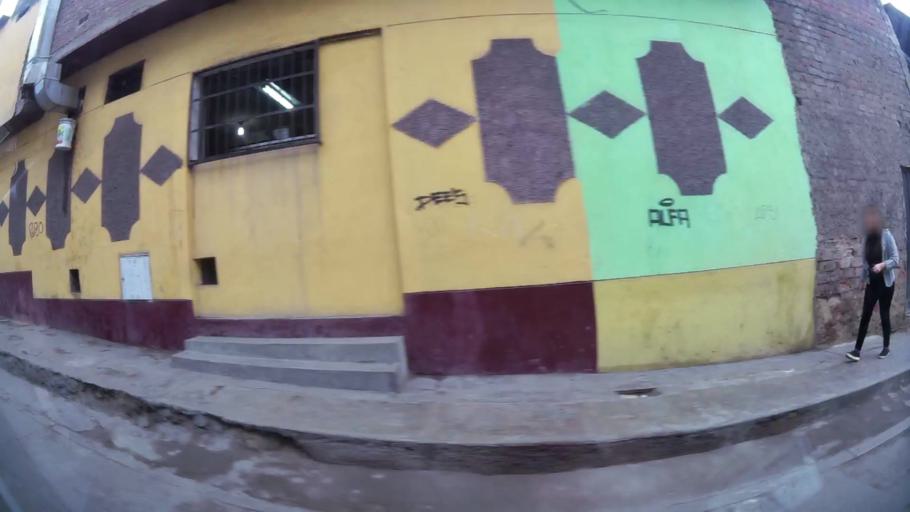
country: PE
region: Lima
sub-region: Lima
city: Surco
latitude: -12.1545
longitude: -76.9530
